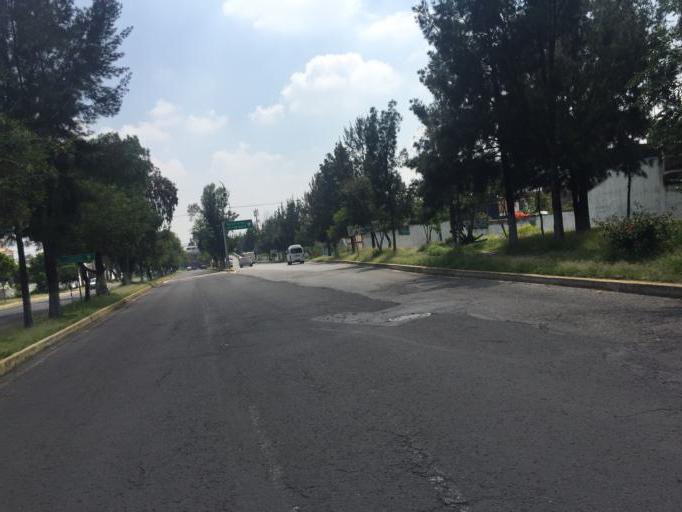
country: MX
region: Mexico
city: Cuautitlan Izcalli
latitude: 19.6487
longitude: -99.2114
